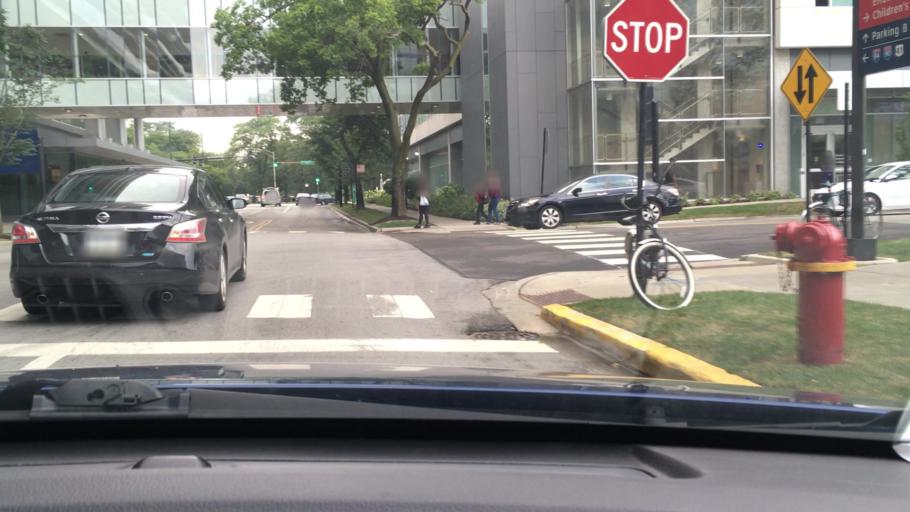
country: US
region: Illinois
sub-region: Cook County
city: Chicago
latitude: 41.7915
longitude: -87.6046
